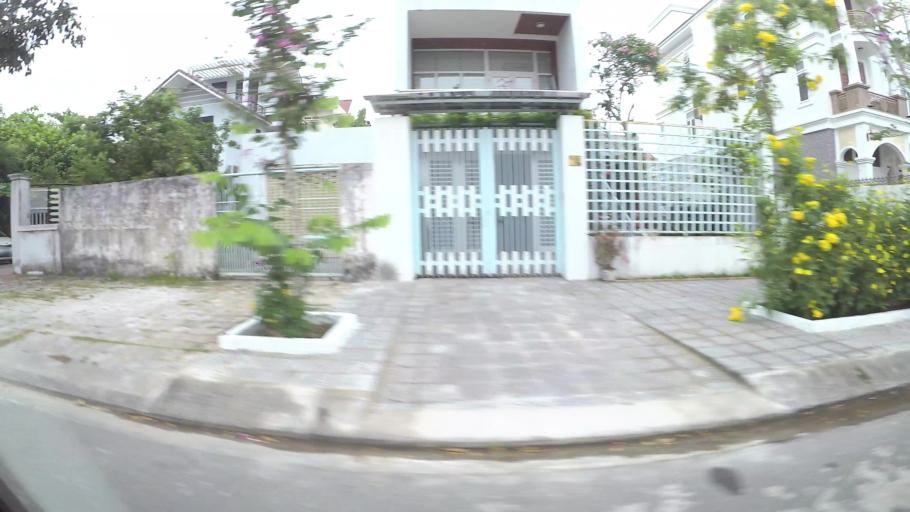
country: VN
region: Da Nang
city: Ngu Hanh Son
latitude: 16.0302
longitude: 108.2307
